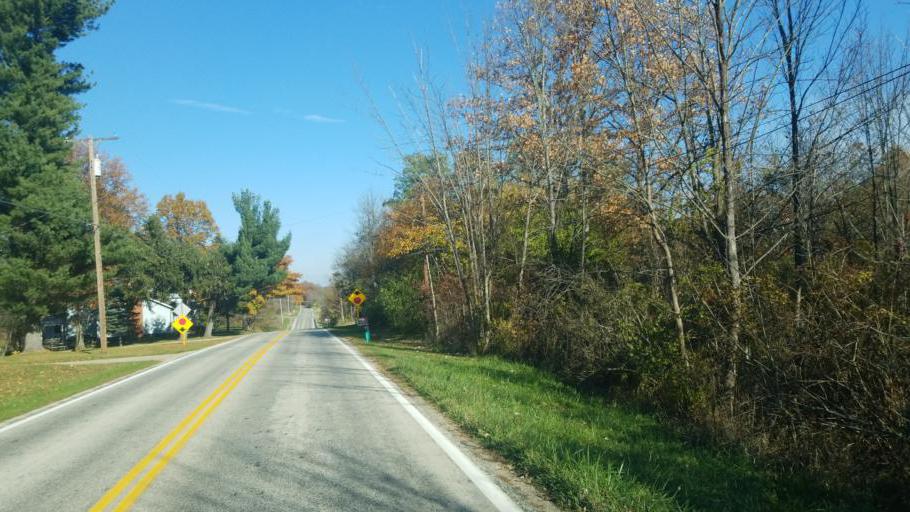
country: US
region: Ohio
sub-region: Ashland County
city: Ashland
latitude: 40.8407
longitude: -82.3178
